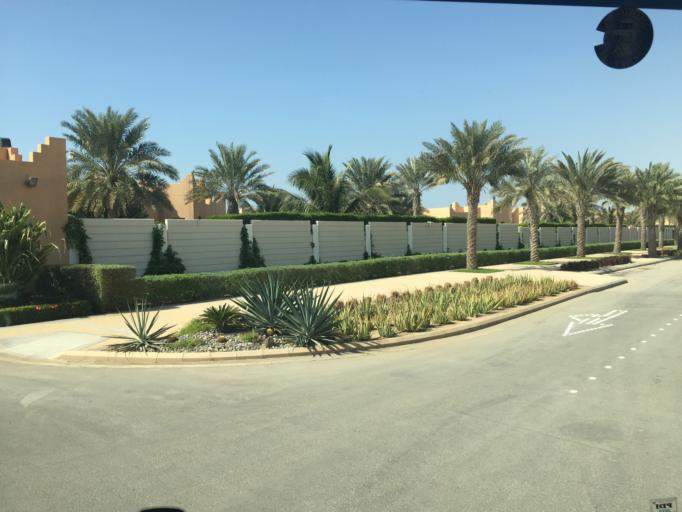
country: SA
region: Makkah
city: Rabigh
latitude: 22.4129
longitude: 39.0787
